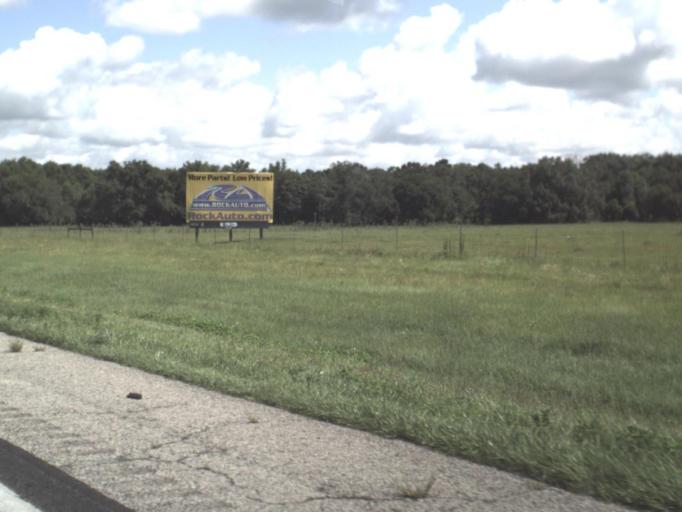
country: US
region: Florida
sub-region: Alachua County
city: Alachua
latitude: 29.7585
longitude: -82.4992
